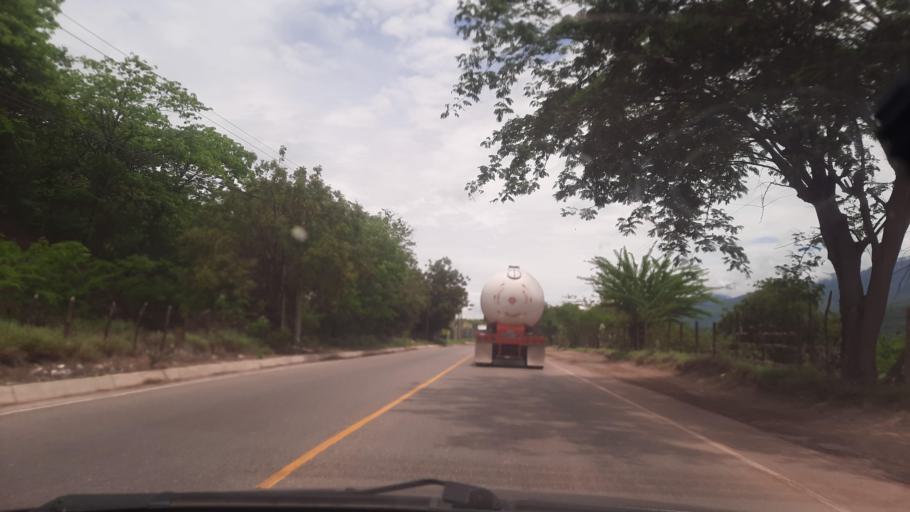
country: GT
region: Zacapa
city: Rio Hondo
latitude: 15.0766
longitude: -89.4944
